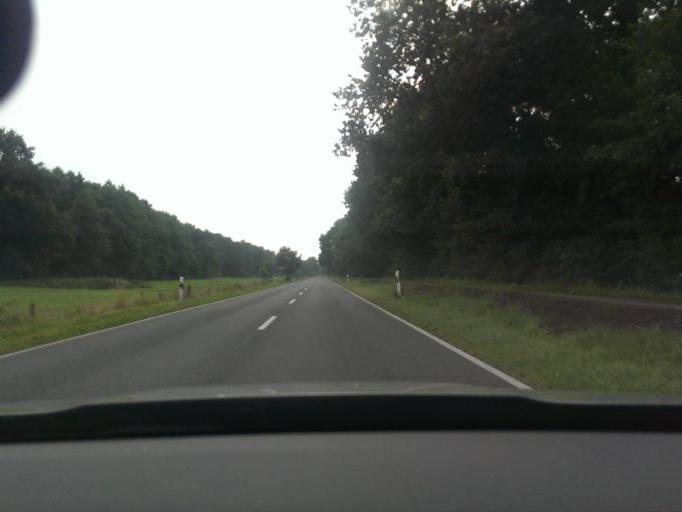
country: DE
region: Lower Saxony
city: Osterholz-Scharmbeck
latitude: 53.1991
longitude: 8.8567
